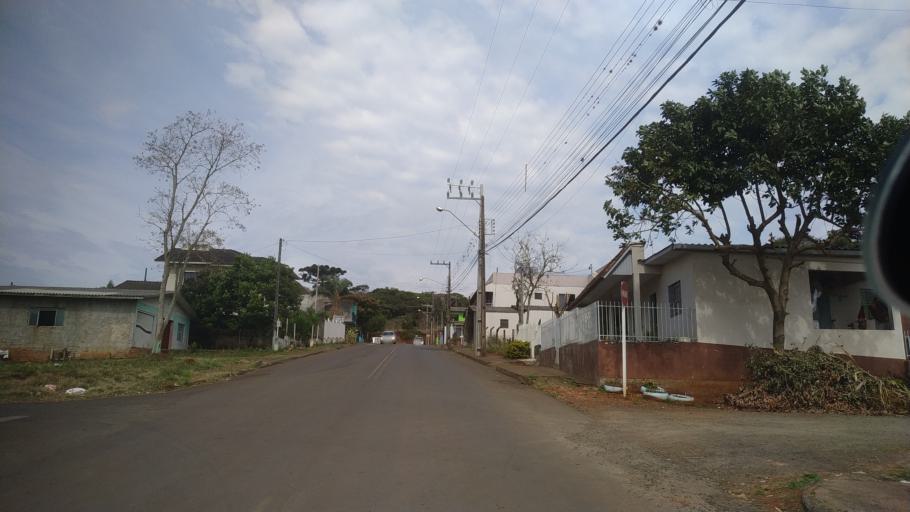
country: BR
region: Santa Catarina
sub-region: Chapeco
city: Chapeco
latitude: -27.1353
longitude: -52.6197
